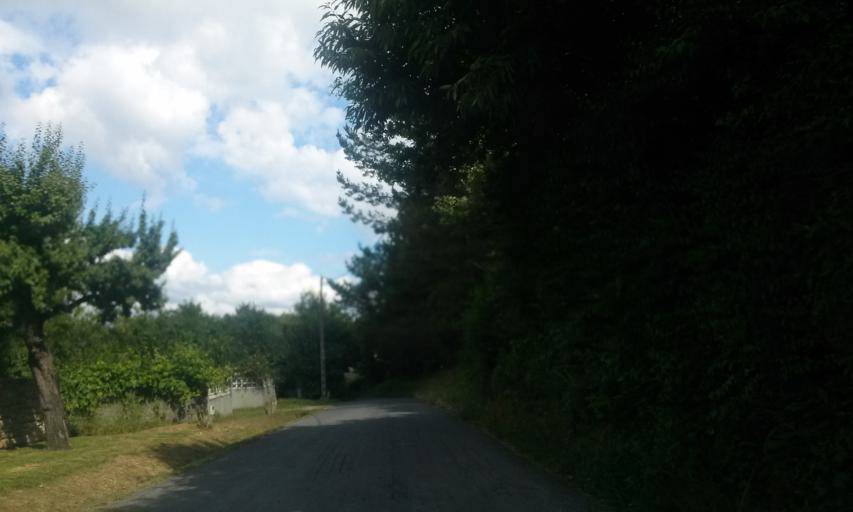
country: ES
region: Galicia
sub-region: Provincia de Lugo
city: Begonte
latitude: 43.1174
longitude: -7.6605
